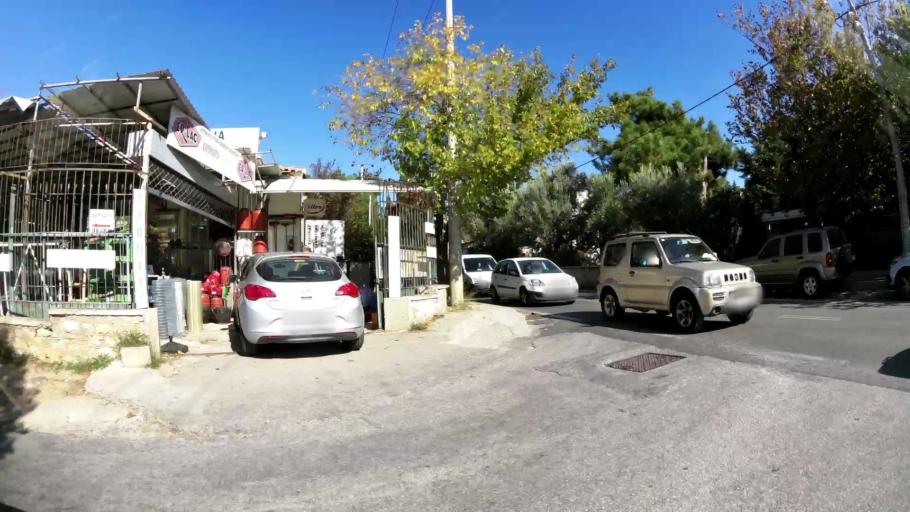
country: GR
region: Attica
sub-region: Nomarchia Athinas
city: Lykovrysi
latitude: 38.0782
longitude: 23.7945
